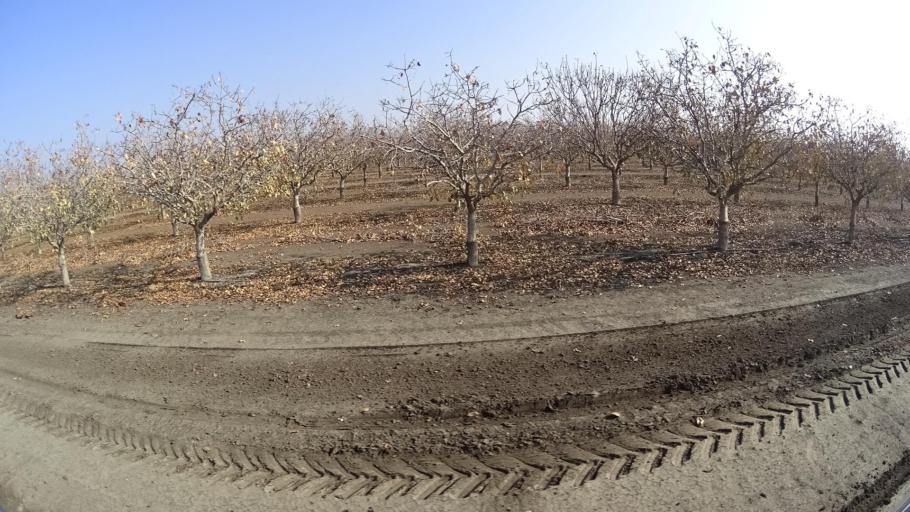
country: US
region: California
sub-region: Kern County
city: Buttonwillow
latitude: 35.3636
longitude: -119.4123
